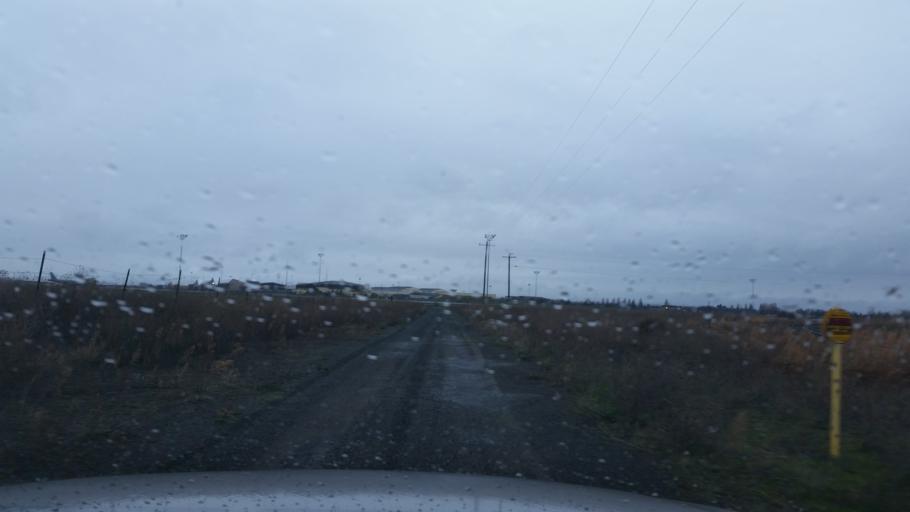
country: US
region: Washington
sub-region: Spokane County
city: Fairchild Air Force Base
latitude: 47.6284
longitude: -117.6236
